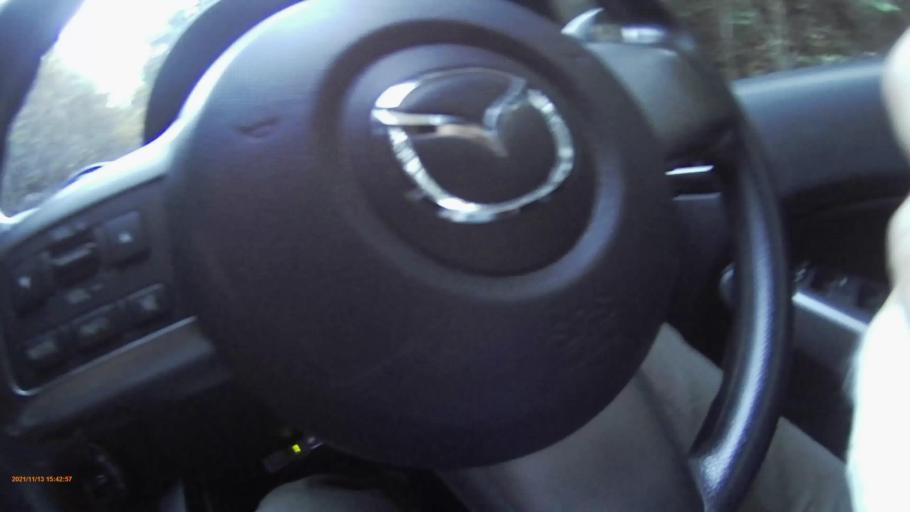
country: JP
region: Gifu
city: Nakatsugawa
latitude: 35.5916
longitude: 137.3925
